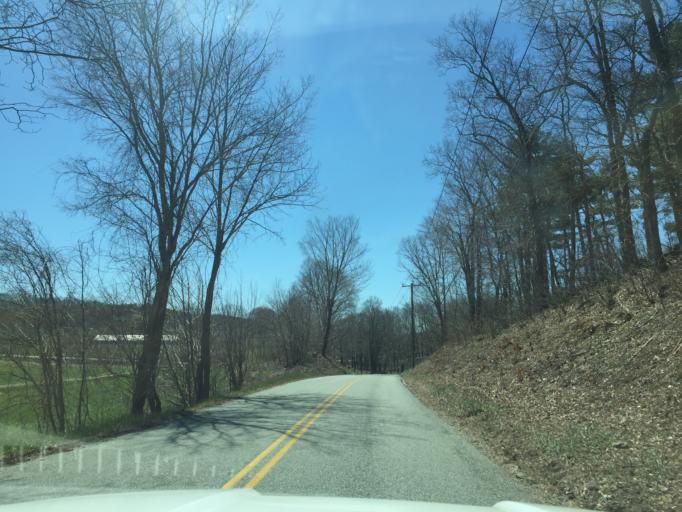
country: US
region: Connecticut
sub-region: Windham County
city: Quinebaug
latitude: 41.9955
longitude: -71.9516
